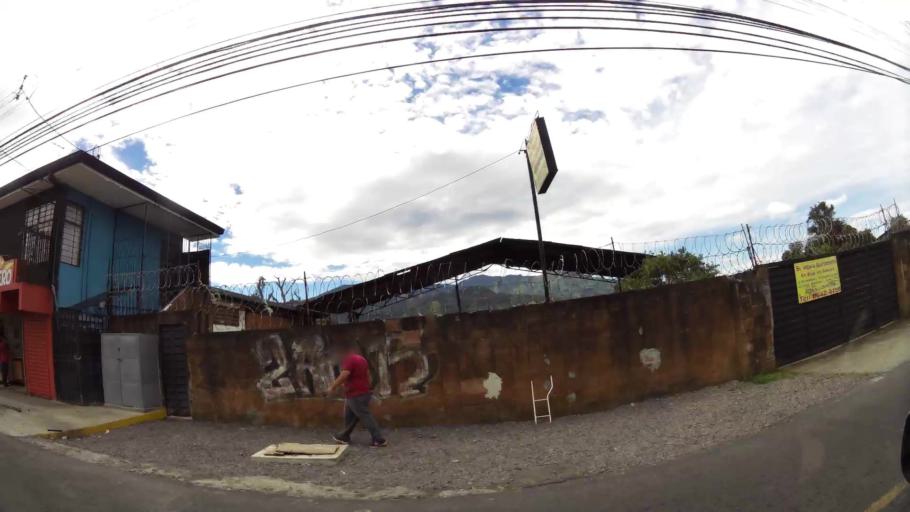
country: CR
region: San Jose
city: San Rafael Arriba
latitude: 9.8902
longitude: -84.0721
